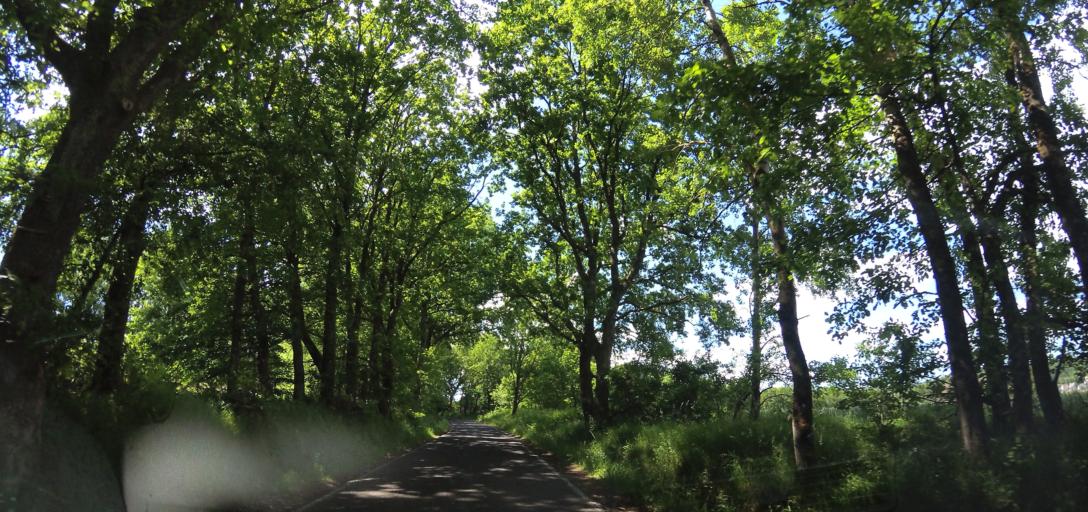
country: DE
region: Saarland
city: Weiskirchen
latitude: 49.5581
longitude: 6.8481
